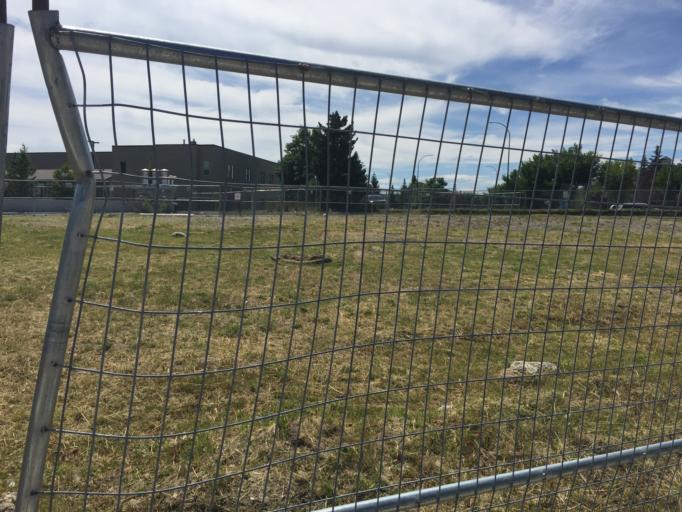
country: CA
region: Alberta
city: Calgary
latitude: 51.0170
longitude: -114.1334
